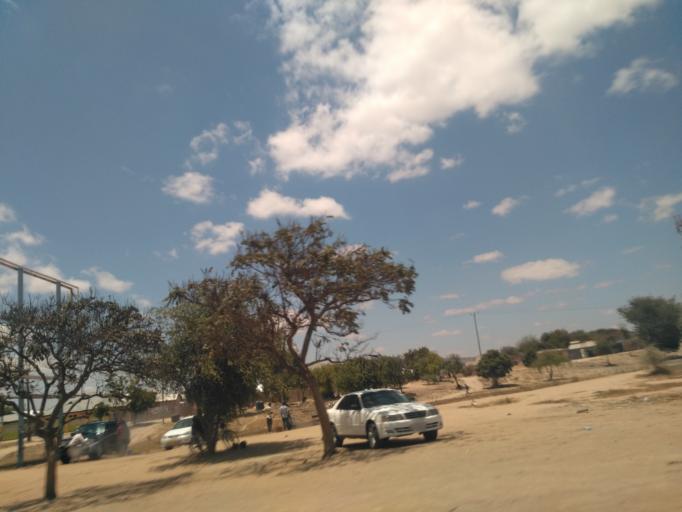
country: TZ
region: Dodoma
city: Dodoma
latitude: -6.1743
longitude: 35.7645
